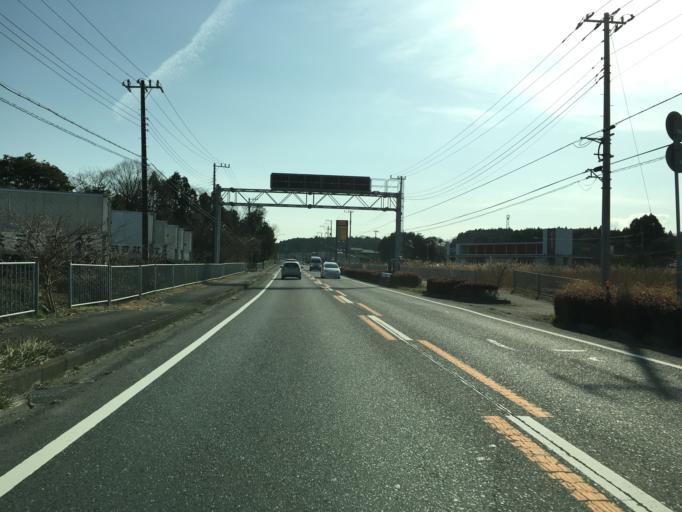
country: JP
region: Ibaraki
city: Takahagi
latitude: 36.7450
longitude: 140.7272
